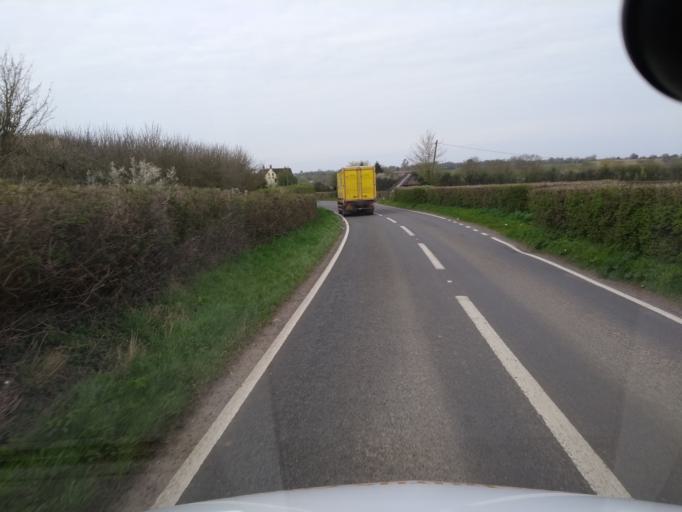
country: GB
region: England
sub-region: Somerset
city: Creech Saint Michael
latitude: 51.0059
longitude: -2.9567
